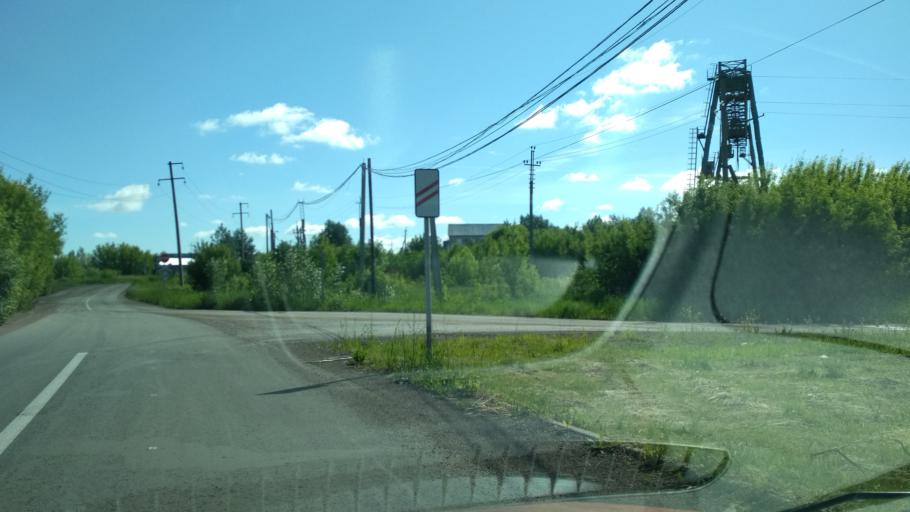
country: RU
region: Tatarstan
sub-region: Tukayevskiy Rayon
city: Naberezhnyye Chelny
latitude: 55.6534
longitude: 52.3010
